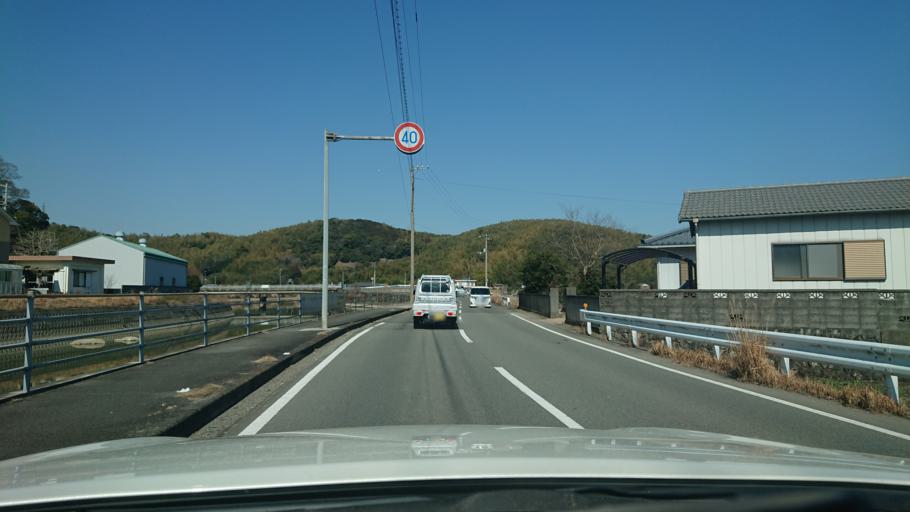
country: JP
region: Tokushima
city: Komatsushimacho
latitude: 33.9685
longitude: 134.6022
